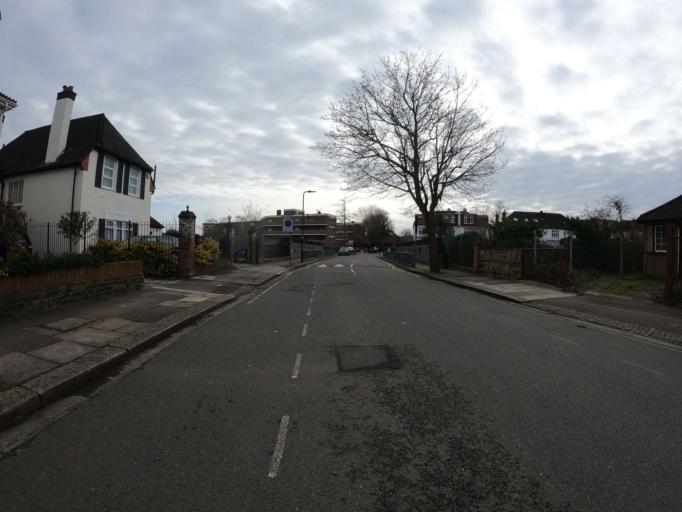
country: GB
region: England
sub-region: Greater London
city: Acton
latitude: 51.5062
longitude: -0.2874
